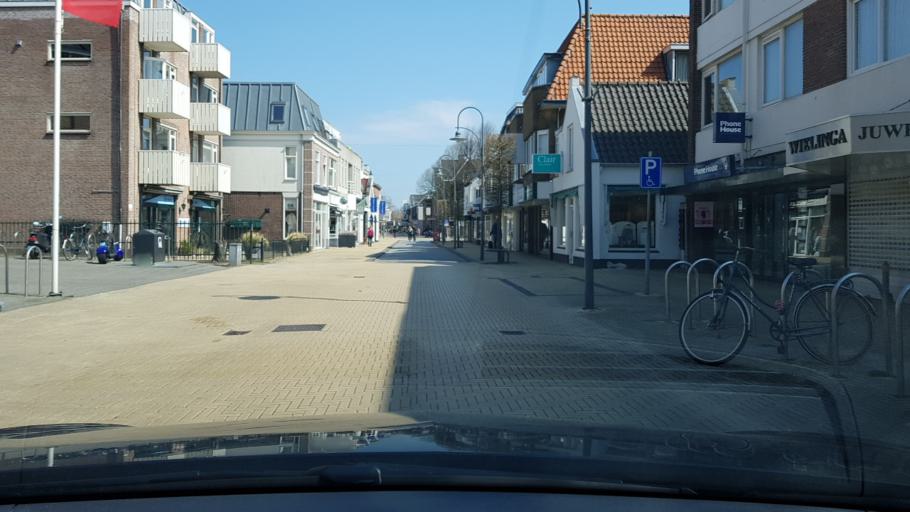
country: NL
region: South Holland
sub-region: Gemeente Teylingen
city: Sassenheim
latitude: 52.2251
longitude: 4.5203
